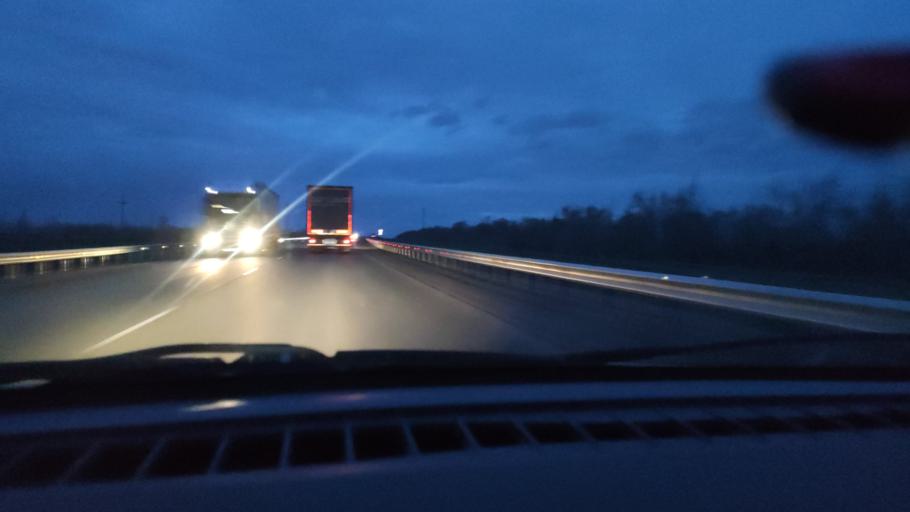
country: RU
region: Orenburg
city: Tatarskaya Kargala
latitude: 51.9846
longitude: 55.1885
